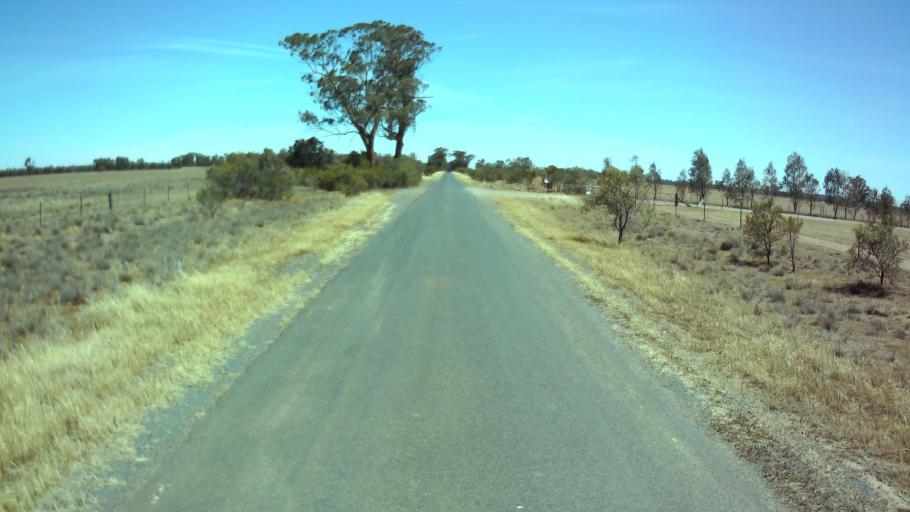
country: AU
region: New South Wales
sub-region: Weddin
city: Grenfell
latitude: -33.8949
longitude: 147.6875
